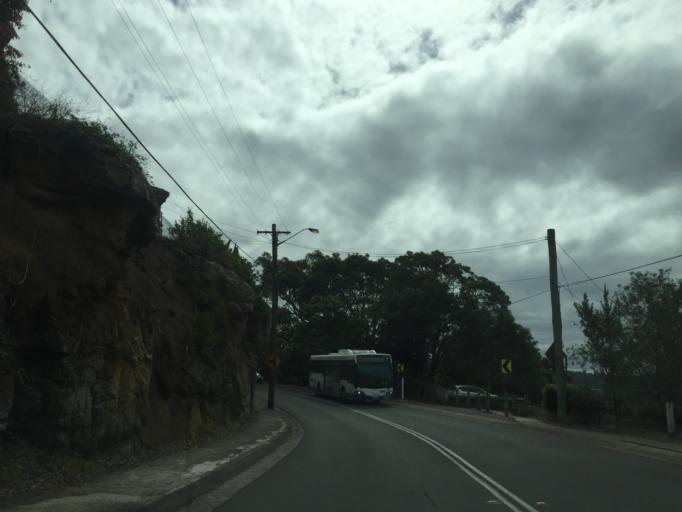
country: AU
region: New South Wales
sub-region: Pittwater
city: North Narrabeen
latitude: -33.6998
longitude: 151.2890
